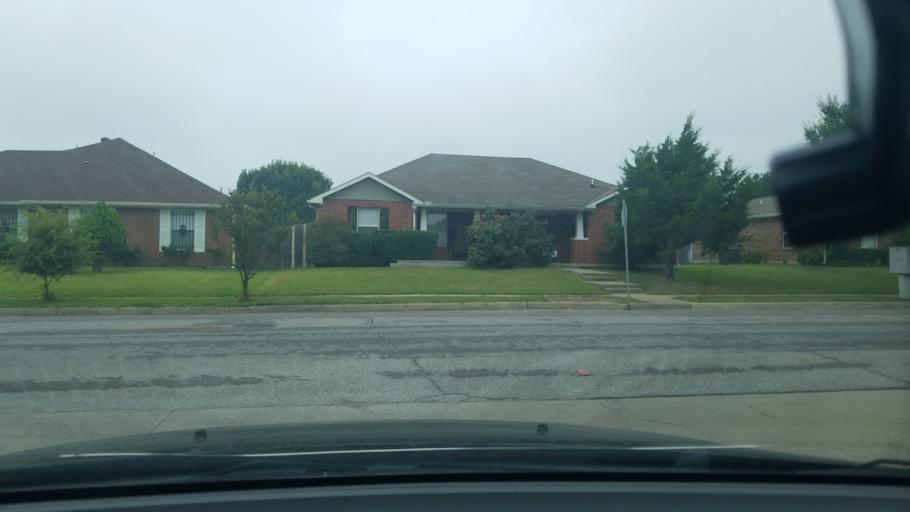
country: US
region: Texas
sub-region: Dallas County
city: Balch Springs
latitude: 32.7553
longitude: -96.6879
